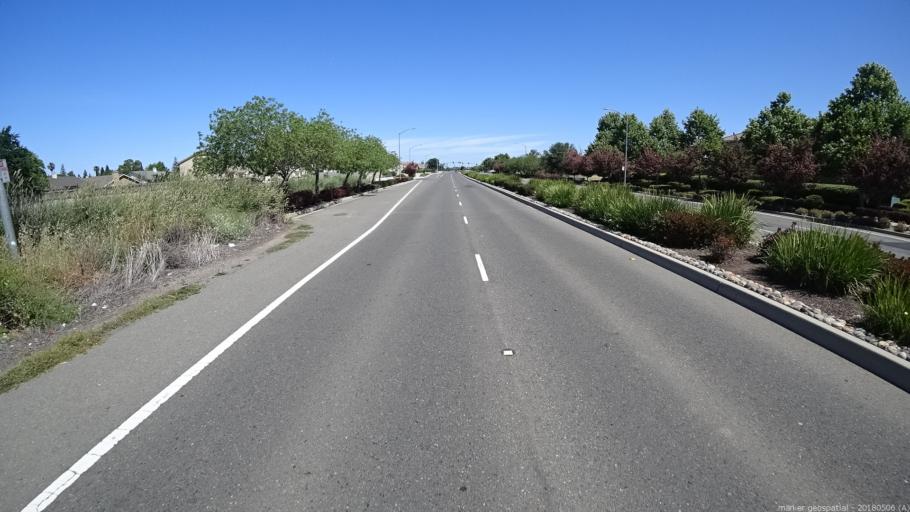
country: US
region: California
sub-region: Sacramento County
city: Laguna
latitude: 38.4411
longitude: -121.4178
